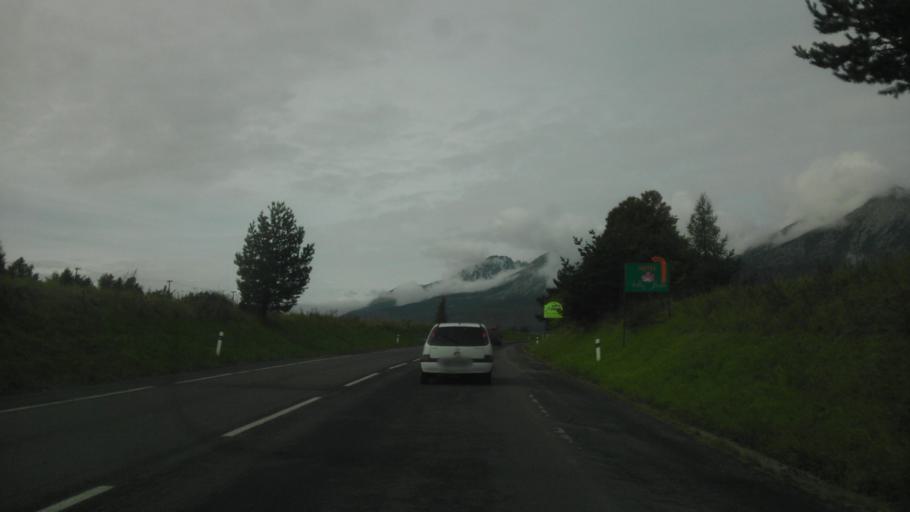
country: SK
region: Presovsky
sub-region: Okres Poprad
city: Nova Lesna
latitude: 49.1165
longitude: 20.2584
